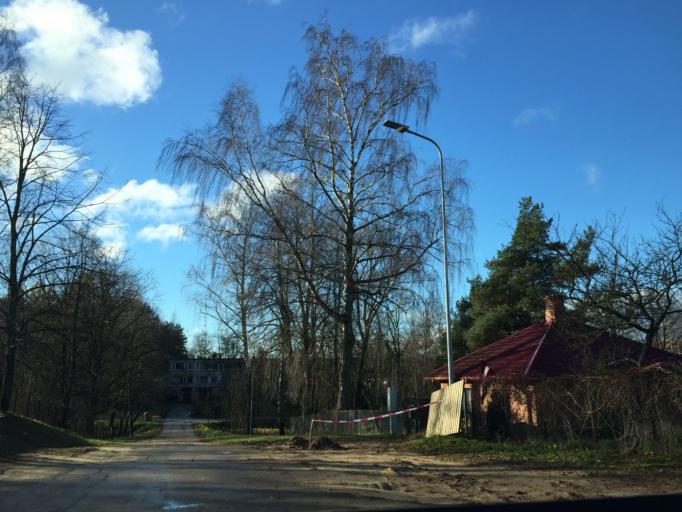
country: LV
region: Valmieras Rajons
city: Valmiera
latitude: 57.5341
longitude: 25.4063
